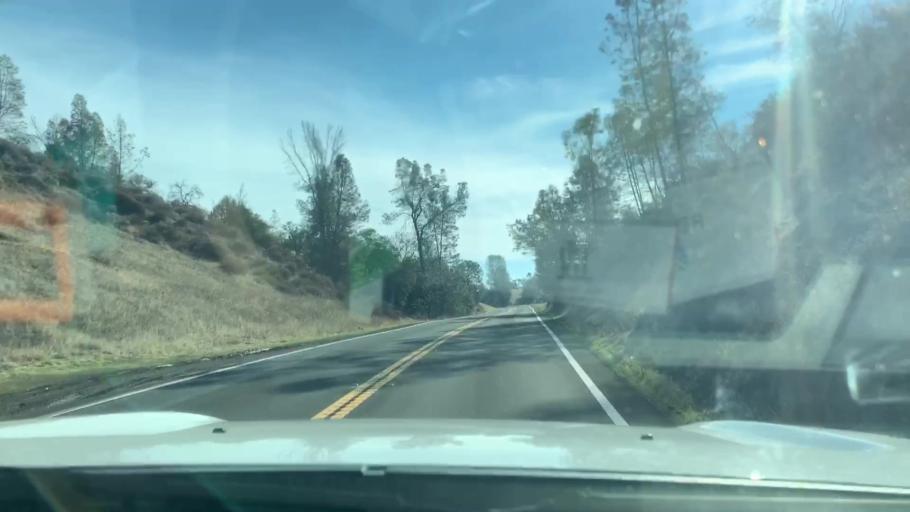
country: US
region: California
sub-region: Fresno County
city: Coalinga
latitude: 36.1135
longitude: -120.5693
